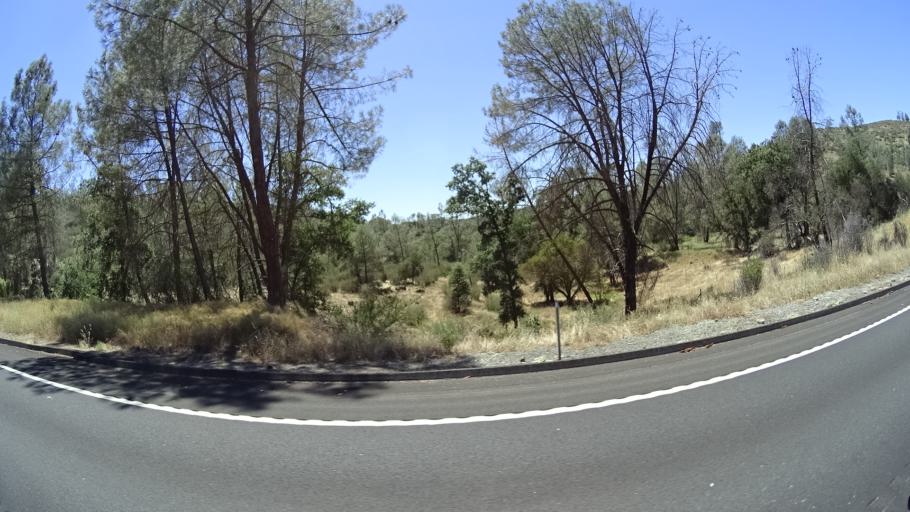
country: US
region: California
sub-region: Calaveras County
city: San Andreas
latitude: 38.2169
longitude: -120.6979
